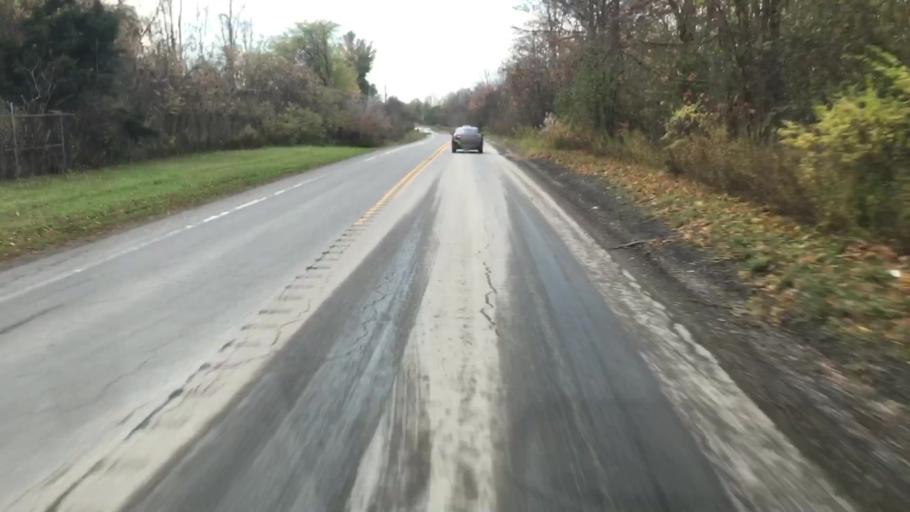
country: US
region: New York
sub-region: Onondaga County
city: Elbridge
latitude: 43.0056
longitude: -76.4203
